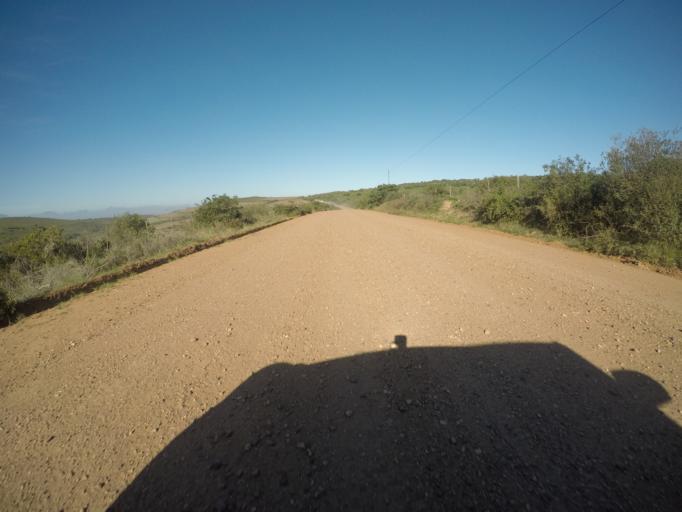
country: ZA
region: Western Cape
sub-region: Eden District Municipality
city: Mossel Bay
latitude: -34.1445
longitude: 22.0075
